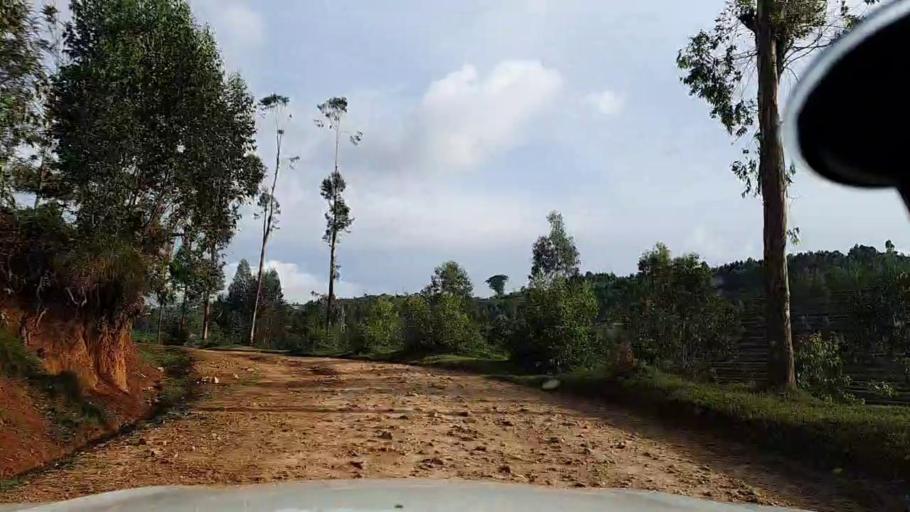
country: RW
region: Southern Province
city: Gitarama
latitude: -2.1810
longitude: 29.5588
